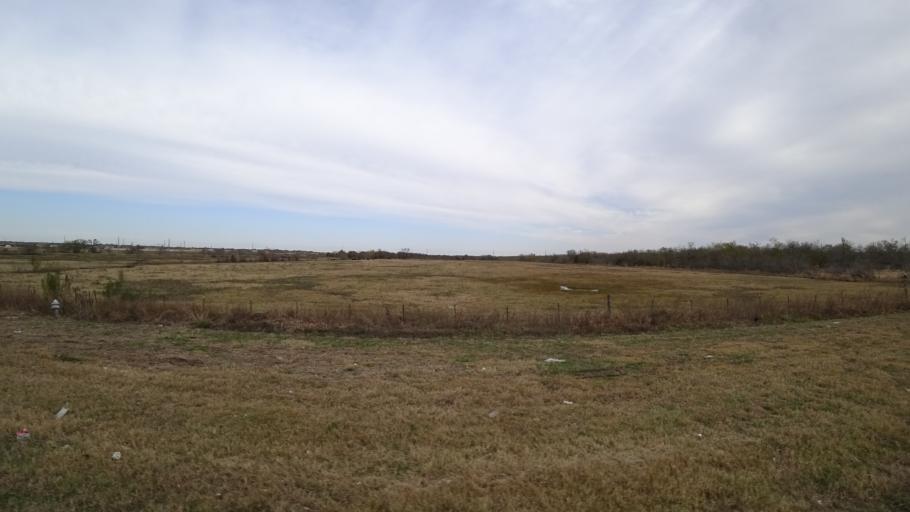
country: US
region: Texas
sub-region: Travis County
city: Garfield
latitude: 30.1511
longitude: -97.6337
